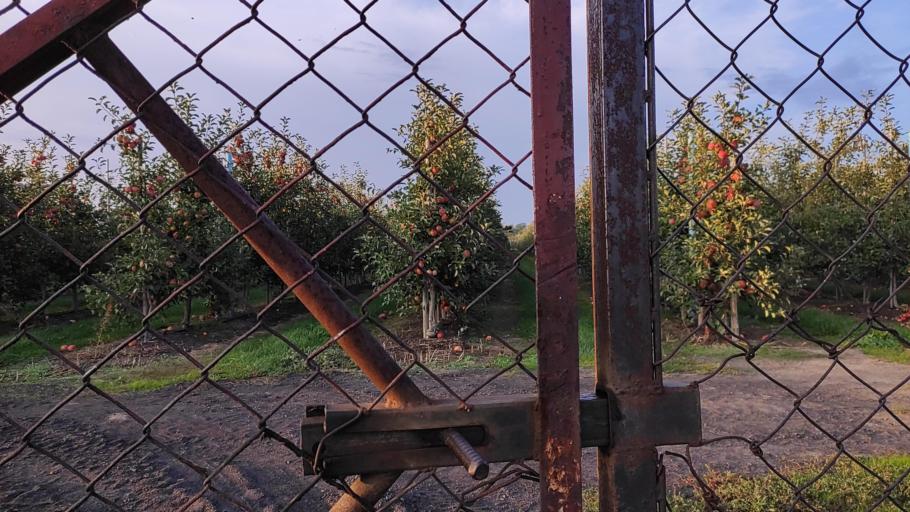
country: PL
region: Greater Poland Voivodeship
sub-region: Powiat poznanski
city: Kostrzyn
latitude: 52.3908
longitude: 17.1788
